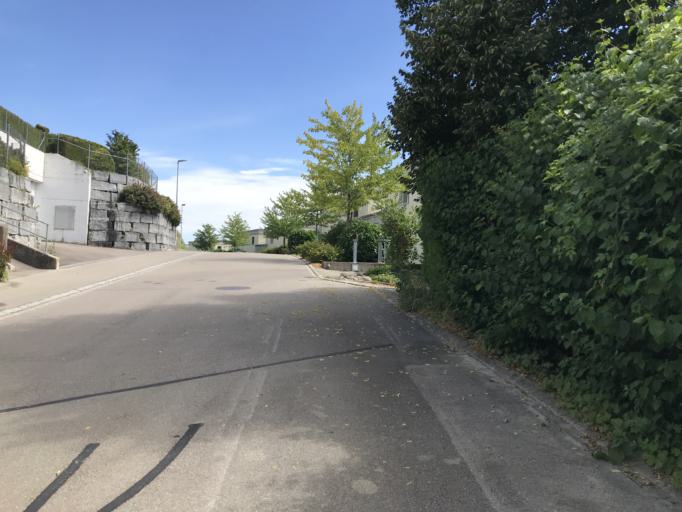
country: CH
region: Zurich
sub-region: Bezirk Winterthur
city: Neftenbach / Dorf Neftenbach
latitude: 47.5209
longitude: 8.6722
